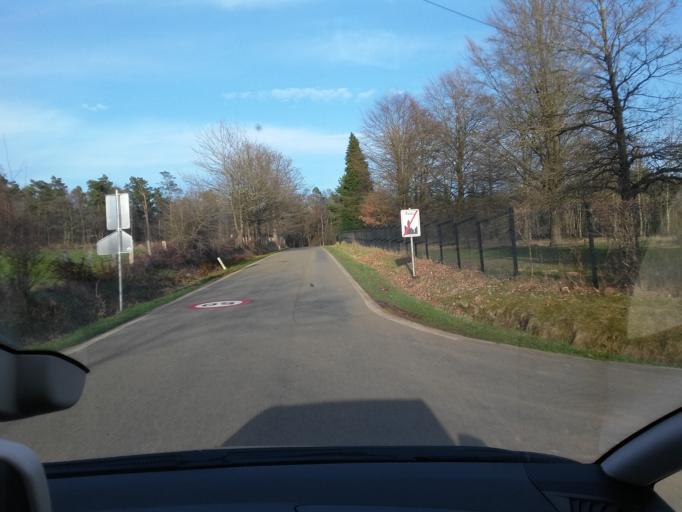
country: BE
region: Wallonia
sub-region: Province du Luxembourg
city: Daverdisse
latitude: 50.0125
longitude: 5.1734
